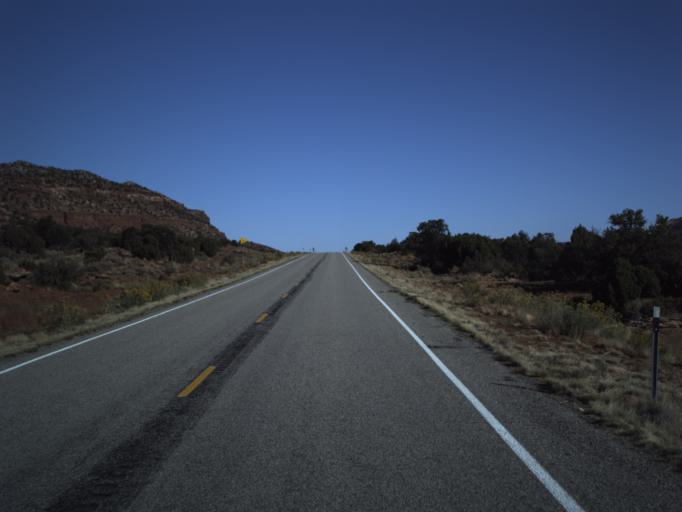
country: US
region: Utah
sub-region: San Juan County
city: Blanding
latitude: 37.6079
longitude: -110.0797
